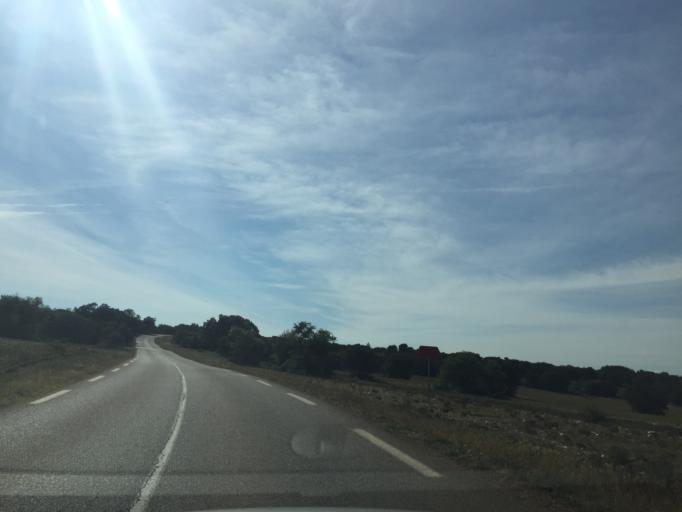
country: FR
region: Provence-Alpes-Cote d'Azur
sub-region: Departement du Var
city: Ginasservis
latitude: 43.6656
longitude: 5.8885
